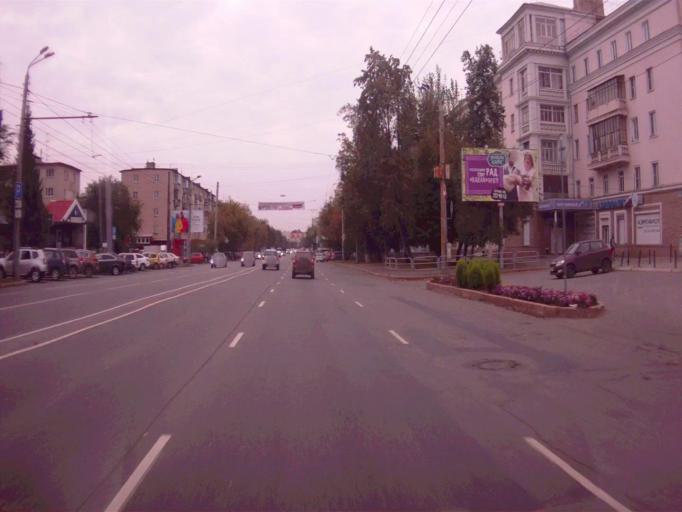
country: RU
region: Chelyabinsk
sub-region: Gorod Chelyabinsk
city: Chelyabinsk
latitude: 55.1532
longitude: 61.4145
